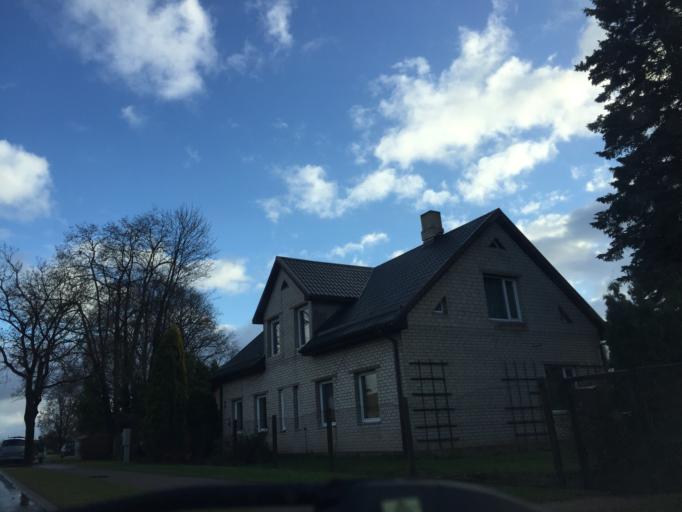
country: LV
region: Valmieras Rajons
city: Valmiera
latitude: 57.5455
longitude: 25.4436
